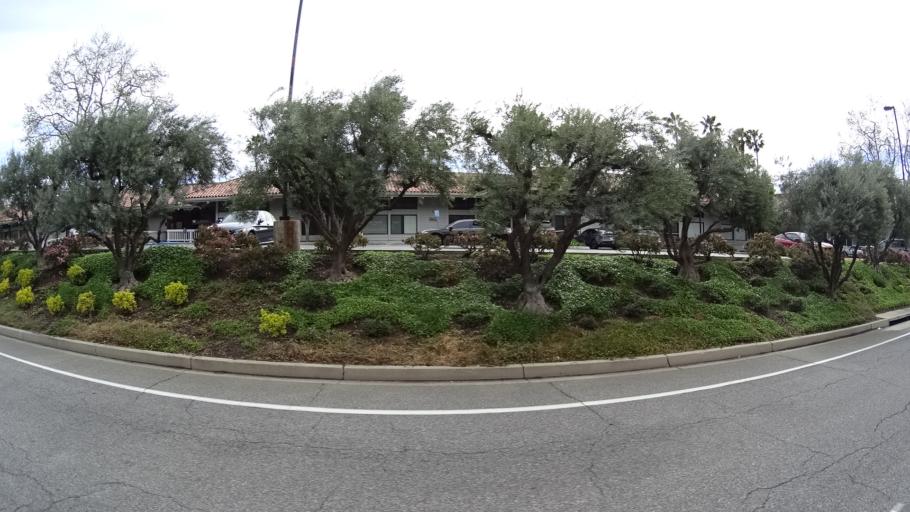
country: US
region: California
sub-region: Ventura County
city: Thousand Oaks
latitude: 34.1550
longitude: -118.8314
